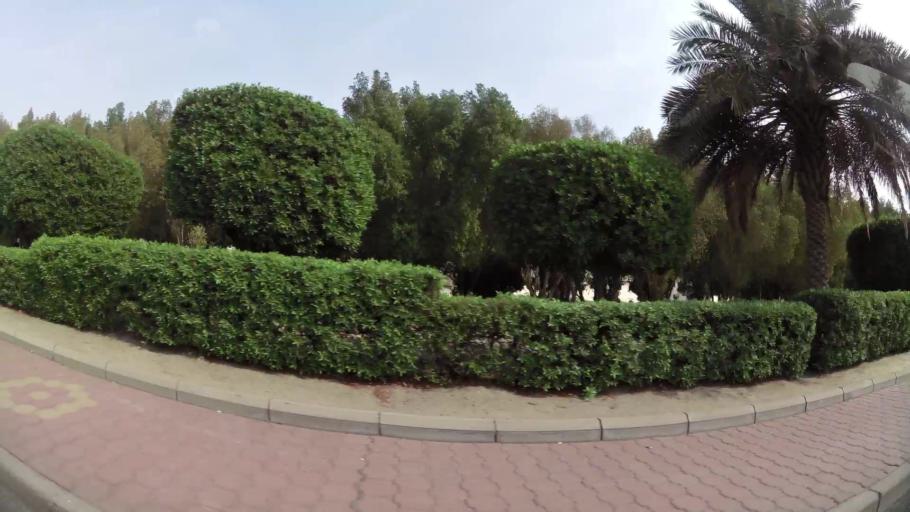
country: KW
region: Al Asimah
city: Ar Rabiyah
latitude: 29.2910
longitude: 47.9284
